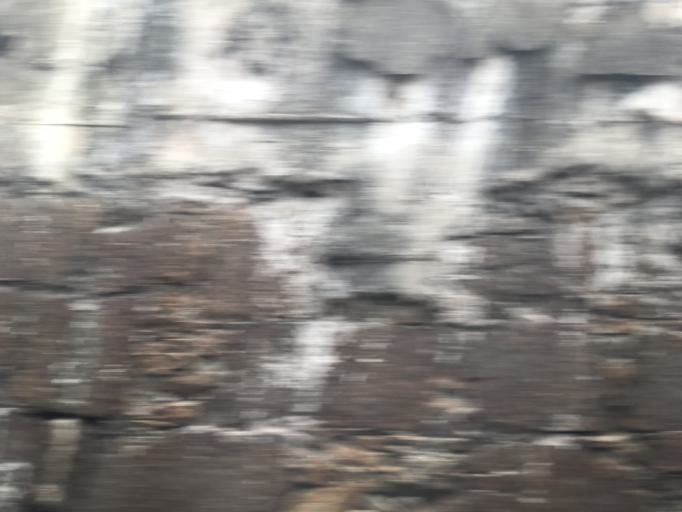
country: BR
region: Rio de Janeiro
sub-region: Rio De Janeiro
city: Rio de Janeiro
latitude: -22.9030
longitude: -43.2769
